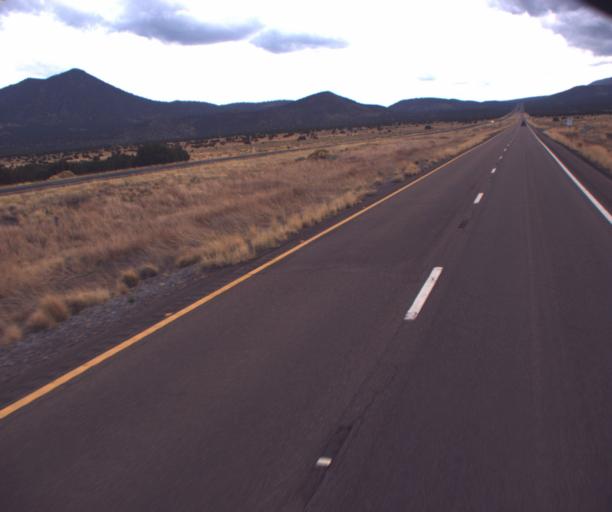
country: US
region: Arizona
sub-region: Coconino County
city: Flagstaff
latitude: 35.4507
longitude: -111.5633
